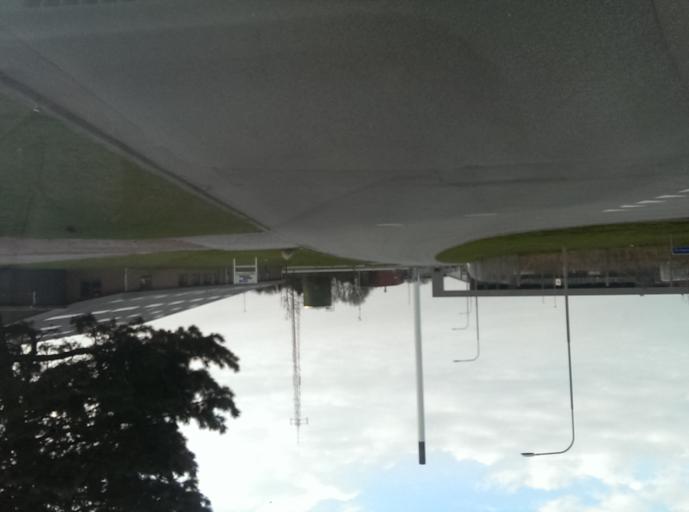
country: DK
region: South Denmark
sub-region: Esbjerg Kommune
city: Esbjerg
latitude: 55.5048
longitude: 8.4091
